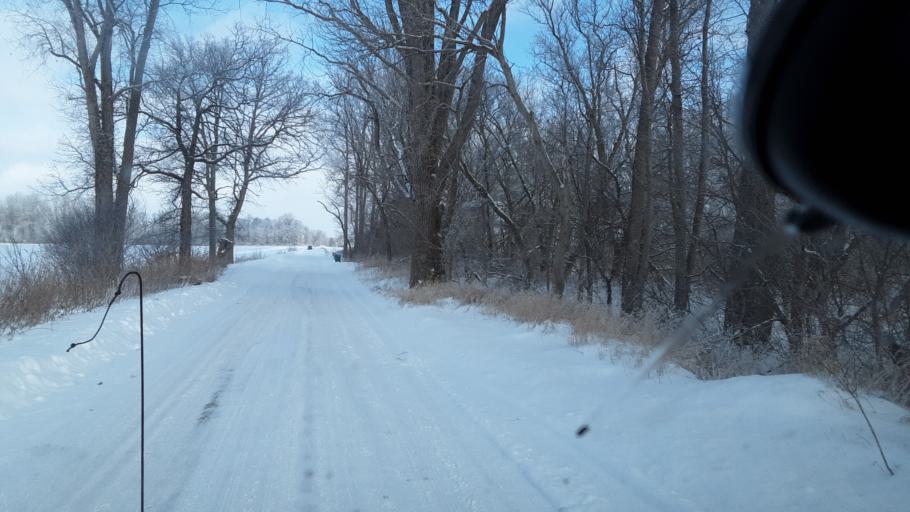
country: US
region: Michigan
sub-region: Eaton County
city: Eaton Rapids
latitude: 42.5153
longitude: -84.6309
